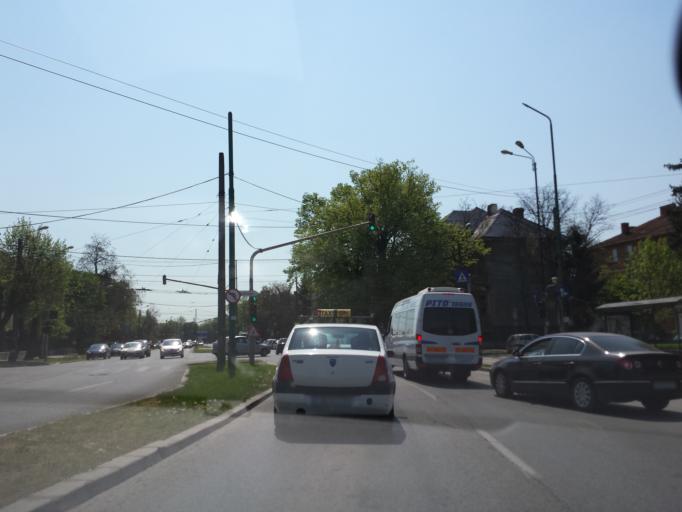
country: RO
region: Timis
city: Timisoara
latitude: 45.7530
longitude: 21.2325
